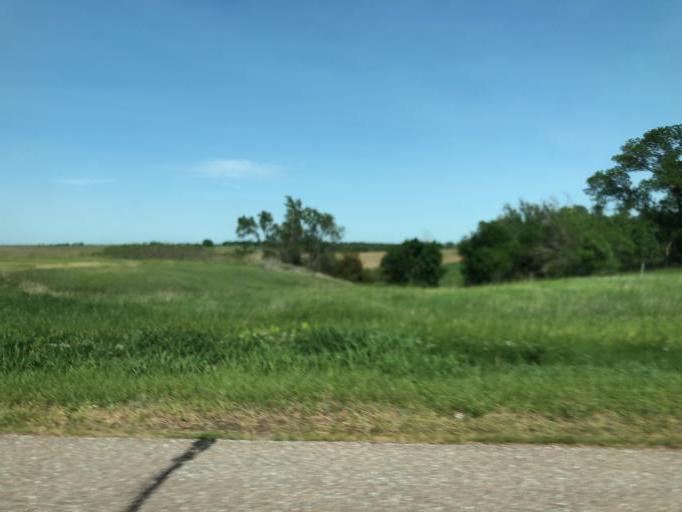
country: US
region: Nebraska
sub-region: York County
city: York
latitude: 40.7713
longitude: -97.5975
